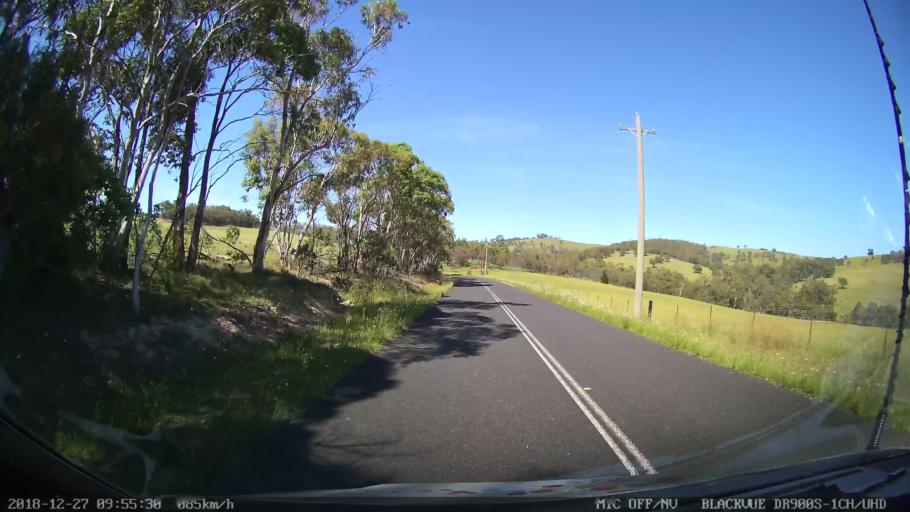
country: AU
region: New South Wales
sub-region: Lithgow
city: Portland
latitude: -33.4021
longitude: 149.9748
